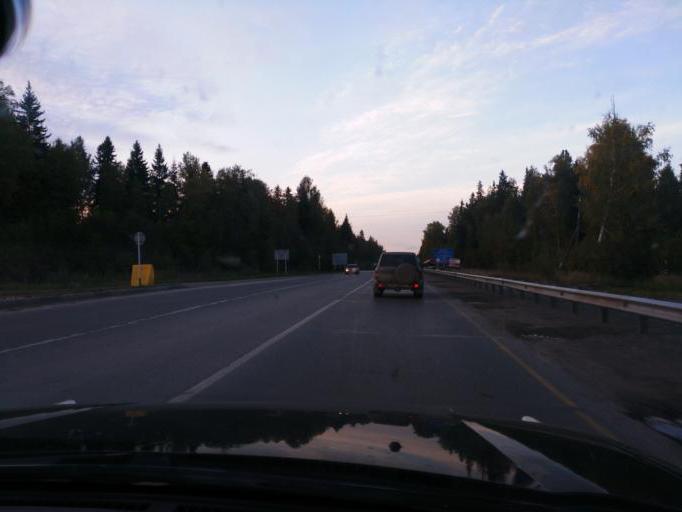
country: RU
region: Perm
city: Polazna
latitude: 58.1386
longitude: 56.4208
